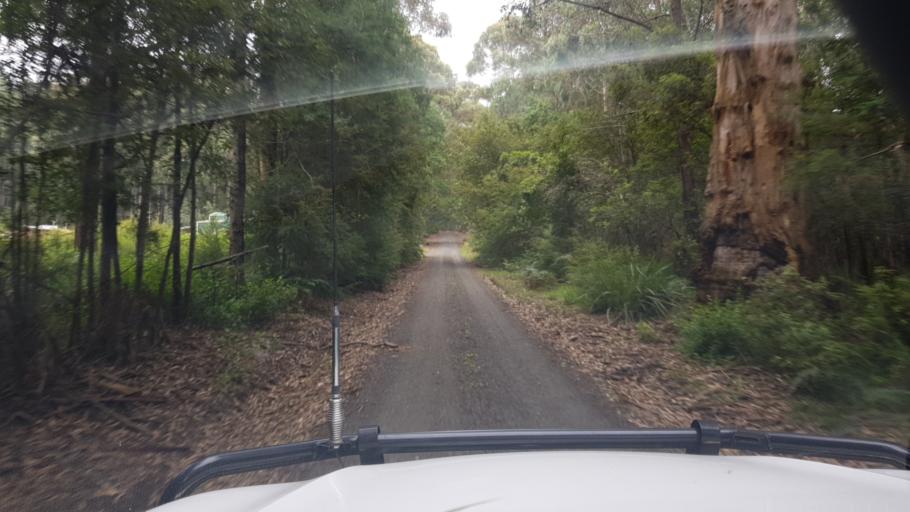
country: AU
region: Victoria
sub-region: Baw Baw
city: Warragul
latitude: -38.0097
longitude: 145.8838
